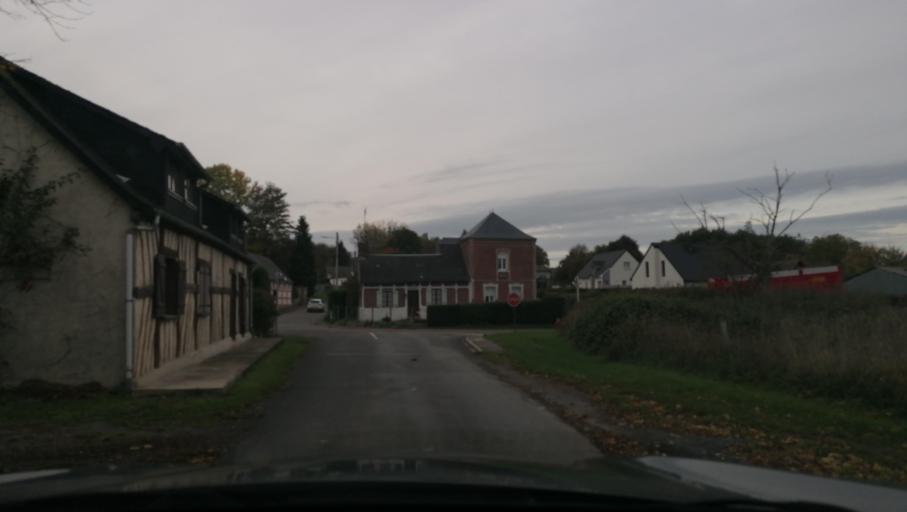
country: FR
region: Picardie
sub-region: Departement de la Somme
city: Bouttencourt
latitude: 49.9045
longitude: 1.6668
